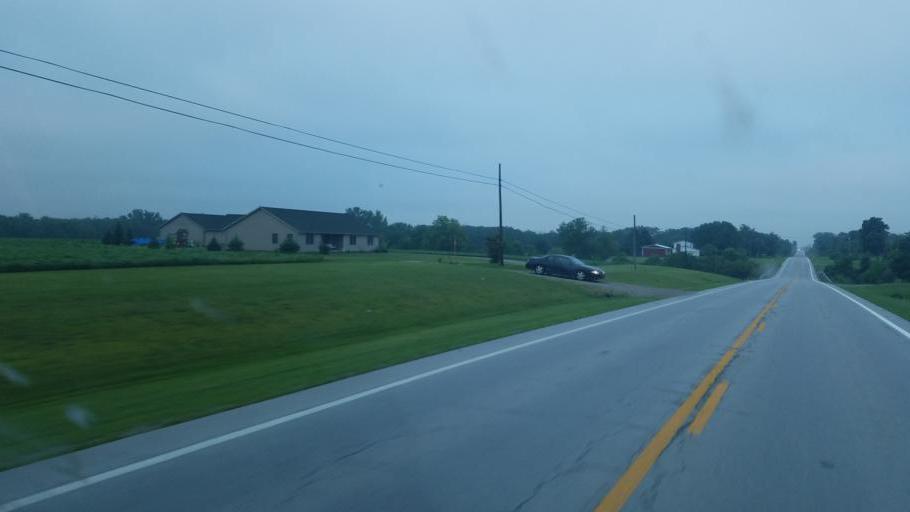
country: US
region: Ohio
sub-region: Madison County
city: Mount Sterling
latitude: 39.6811
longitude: -83.3016
